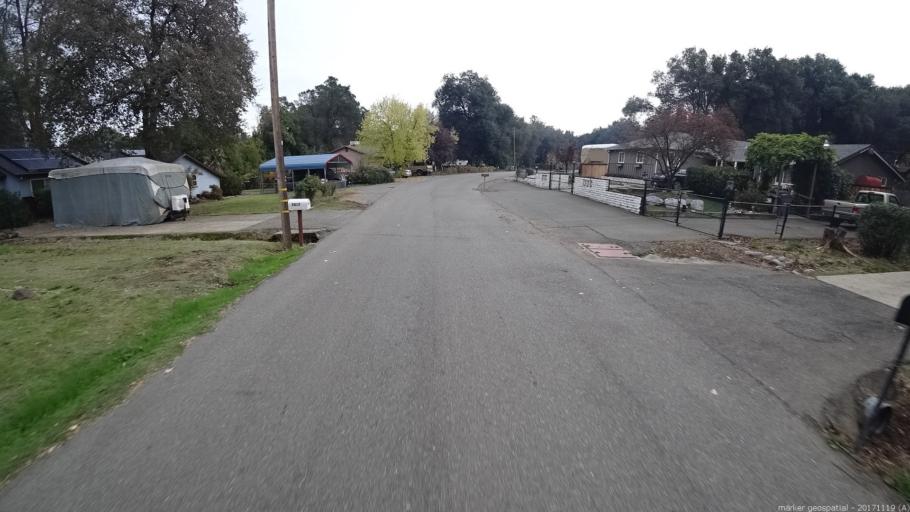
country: US
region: California
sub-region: Shasta County
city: Anderson
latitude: 40.4888
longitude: -122.3710
